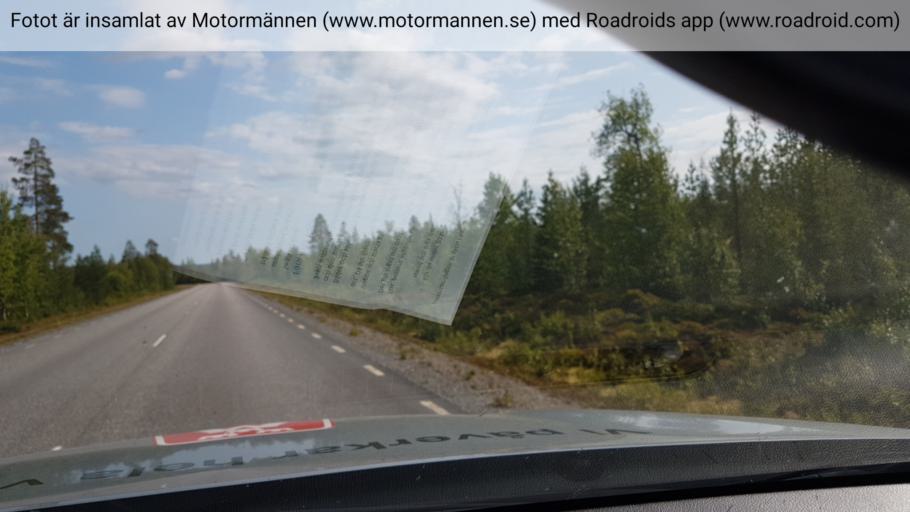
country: SE
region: Vaesterbotten
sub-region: Skelleftea Kommun
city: Storvik
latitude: 65.3413
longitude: 20.5203
